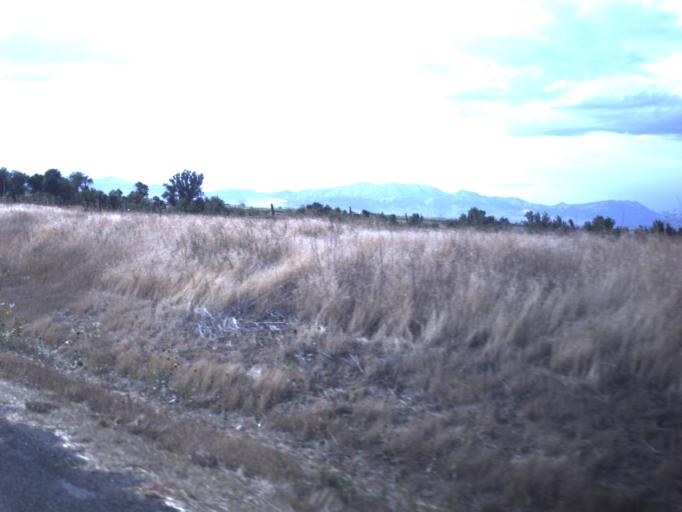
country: US
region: Utah
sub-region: Cache County
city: Lewiston
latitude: 41.9761
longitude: -111.8250
